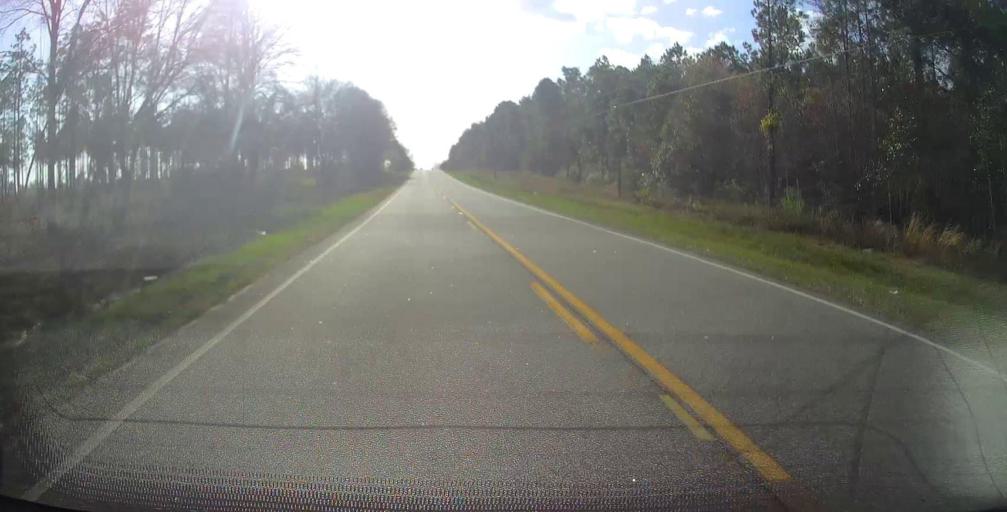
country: US
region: Georgia
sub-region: Wheeler County
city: Alamo
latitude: 32.1697
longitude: -82.6962
